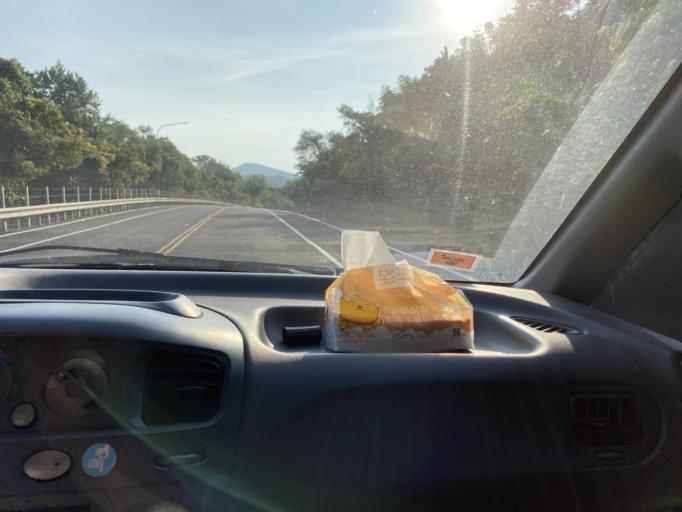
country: TW
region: Taiwan
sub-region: Keelung
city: Keelung
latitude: 25.0348
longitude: 121.8594
